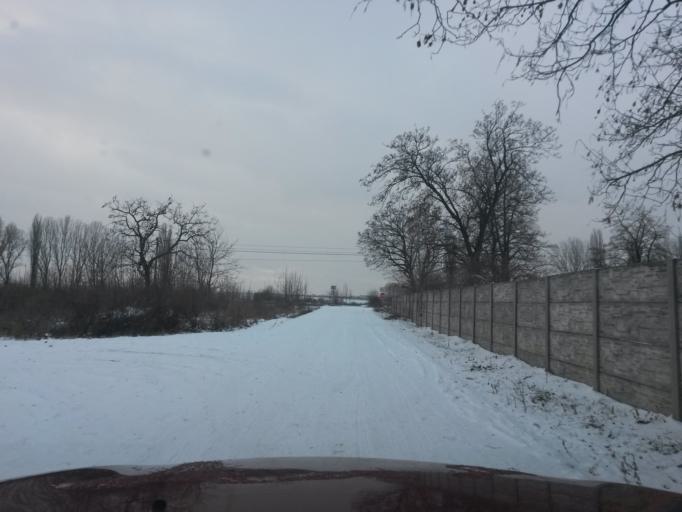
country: SK
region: Kosicky
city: Kosice
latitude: 48.6353
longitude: 21.2942
